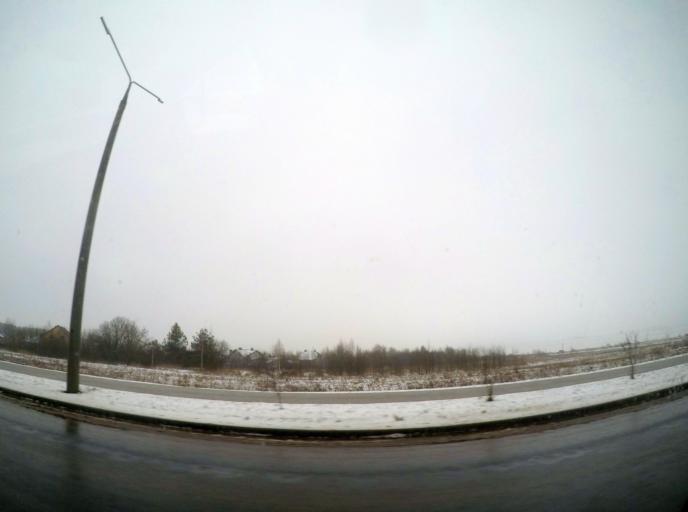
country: BY
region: Grodnenskaya
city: Hrodna
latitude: 53.6120
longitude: 23.8209
